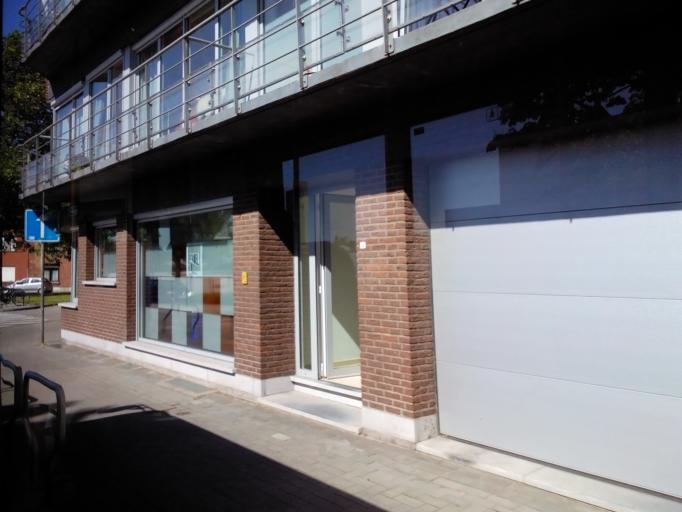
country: BE
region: Flanders
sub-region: Provincie Vlaams-Brabant
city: Leuven
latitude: 50.8870
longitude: 4.7189
